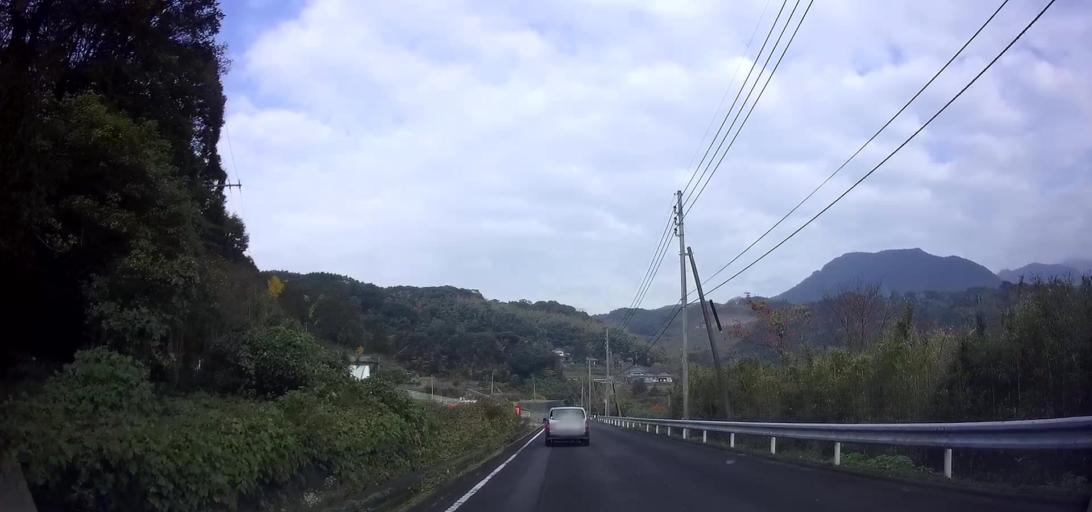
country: JP
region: Nagasaki
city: Shimabara
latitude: 32.6850
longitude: 130.2748
